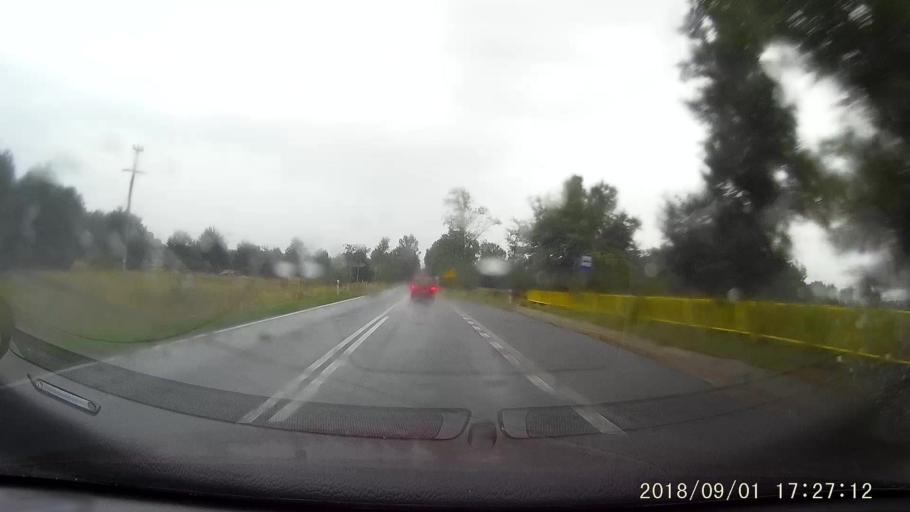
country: PL
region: Lubusz
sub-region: Powiat zaganski
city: Zagan
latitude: 51.6669
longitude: 15.3112
